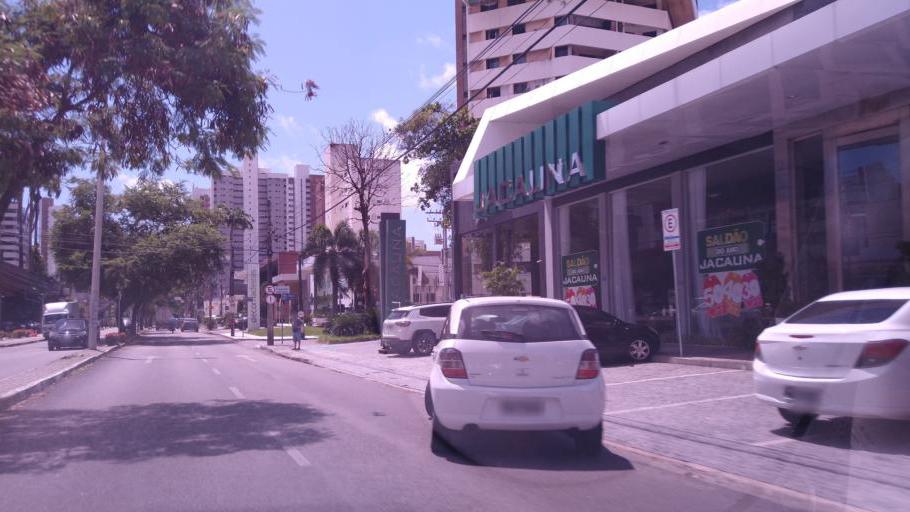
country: BR
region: Ceara
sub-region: Fortaleza
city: Fortaleza
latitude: -3.7333
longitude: -38.4920
